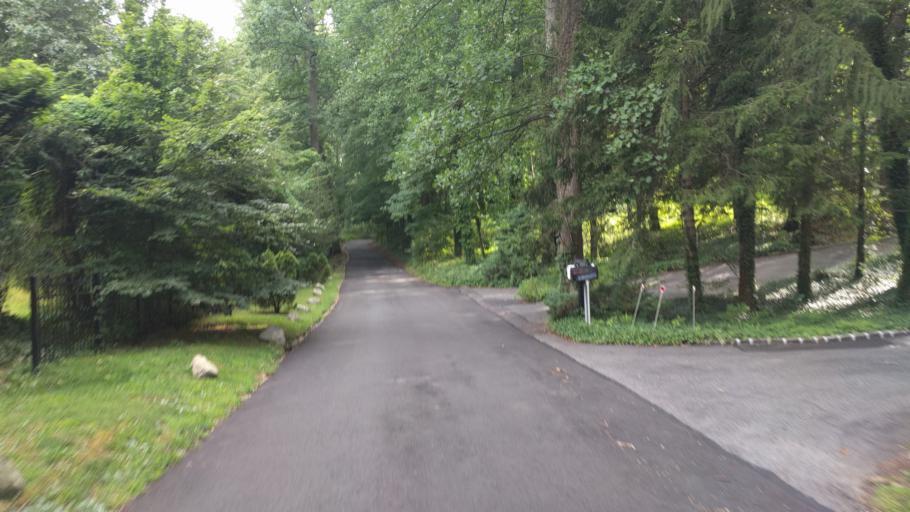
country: US
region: New York
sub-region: Nassau County
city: Oyster Bay Cove
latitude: 40.8691
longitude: -73.4904
